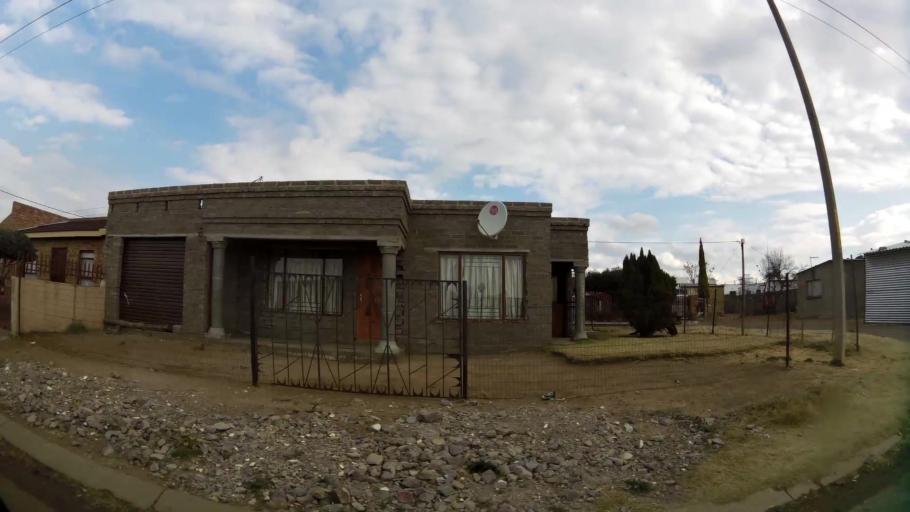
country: ZA
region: Gauteng
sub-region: Sedibeng District Municipality
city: Vanderbijlpark
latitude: -26.6766
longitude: 27.8566
